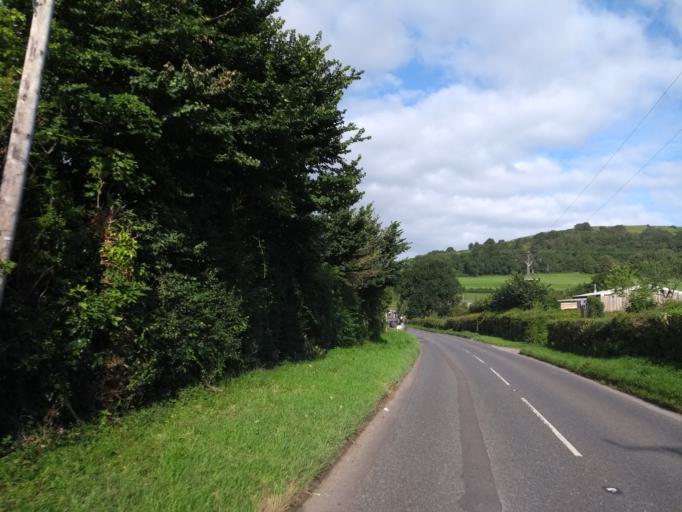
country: GB
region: England
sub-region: Somerset
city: Axbridge
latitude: 51.2892
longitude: -2.8306
